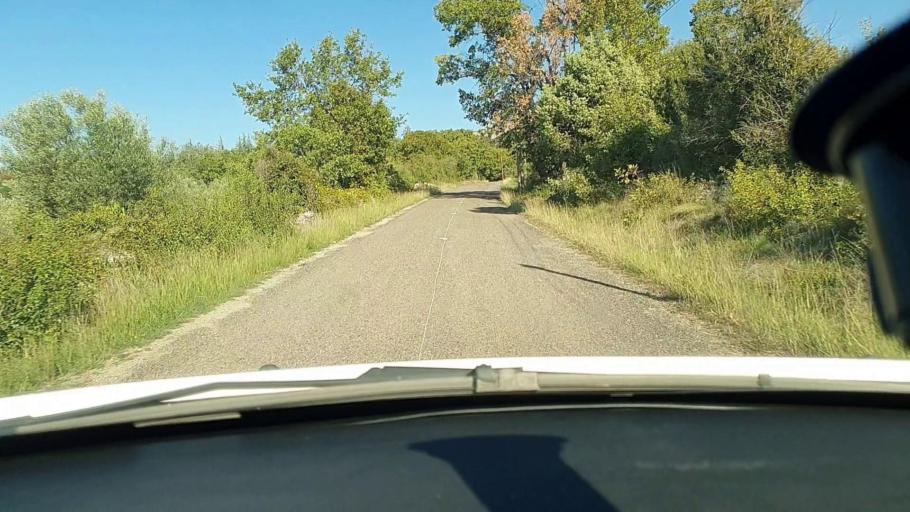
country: FR
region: Languedoc-Roussillon
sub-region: Departement du Gard
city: Barjac
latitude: 44.1898
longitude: 4.3230
